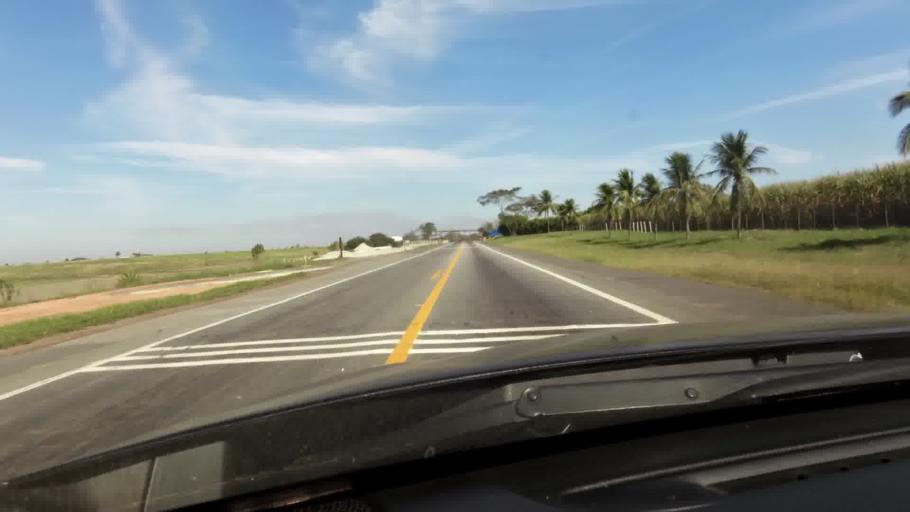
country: BR
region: Rio de Janeiro
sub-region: Campos Dos Goytacazes
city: Campos
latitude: -21.5338
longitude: -41.3407
